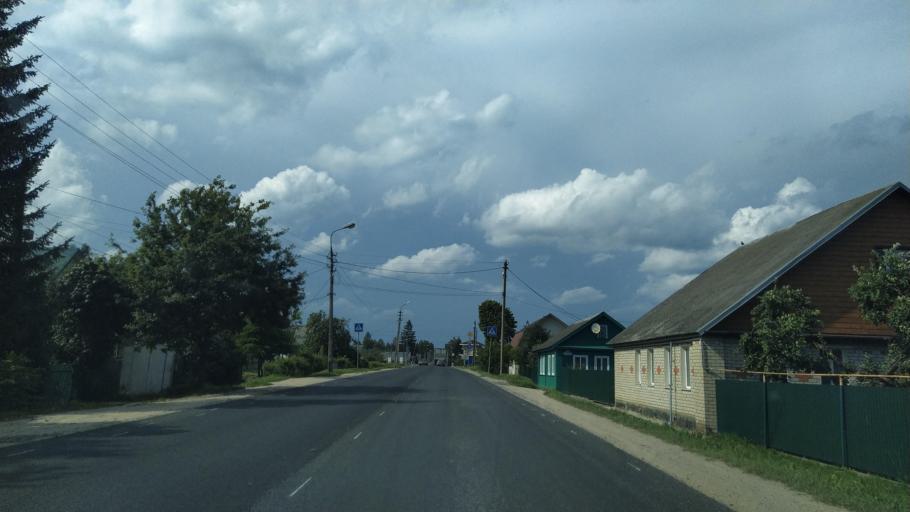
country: RU
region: Pskov
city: Porkhov
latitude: 57.7713
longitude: 29.5514
